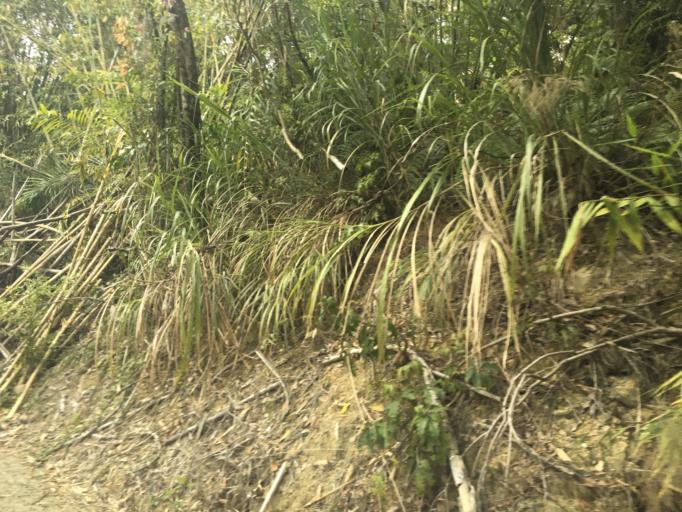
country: TW
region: Taiwan
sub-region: Taichung City
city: Taichung
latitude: 24.1355
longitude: 120.8247
